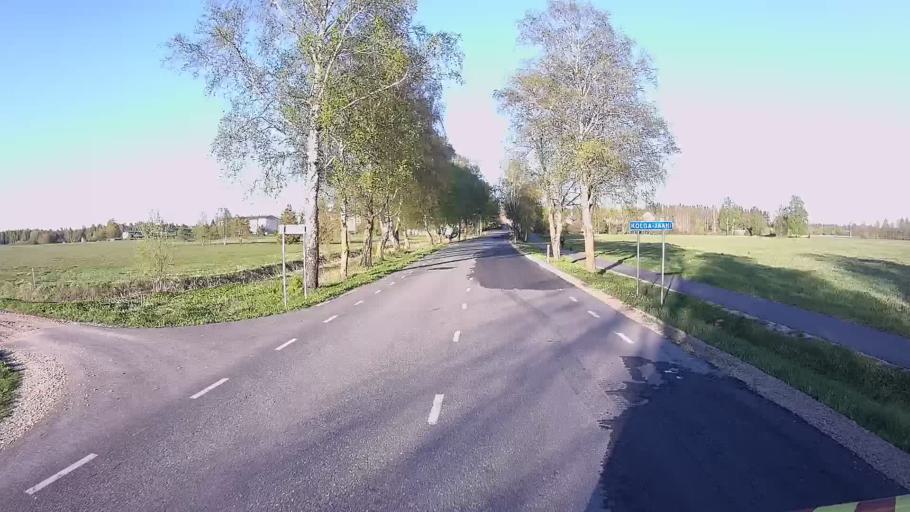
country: EE
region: Jogevamaa
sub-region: Poltsamaa linn
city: Poltsamaa
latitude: 58.5344
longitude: 25.9349
